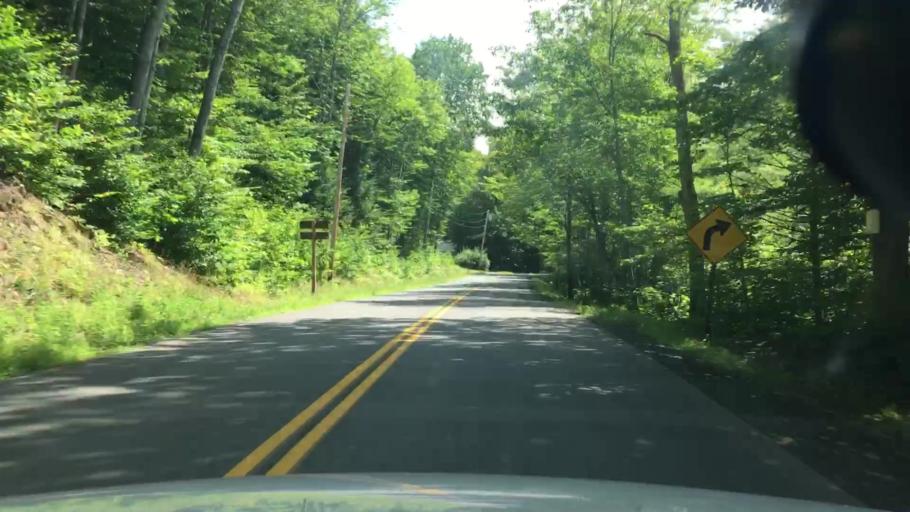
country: US
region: Maine
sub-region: Somerset County
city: Skowhegan
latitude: 44.7229
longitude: -69.7026
